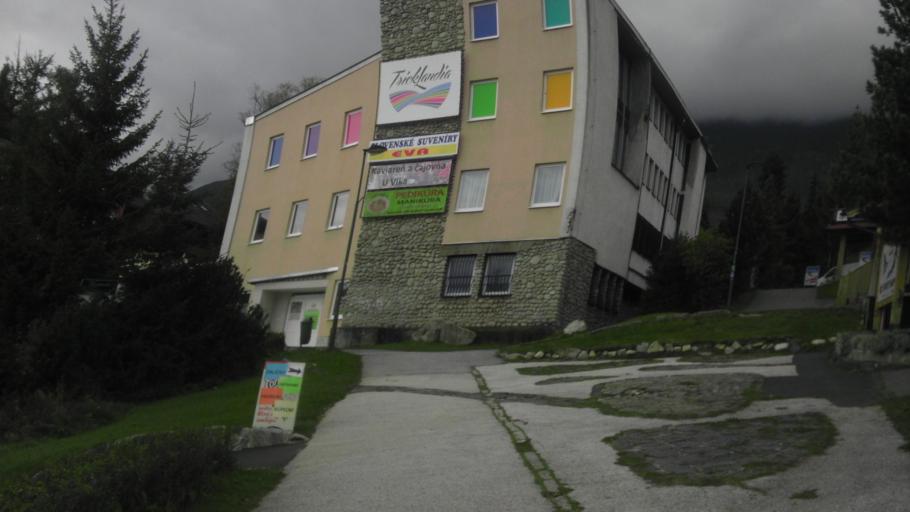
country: SK
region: Presovsky
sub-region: Okres Poprad
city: Vysoke Tatry
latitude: 49.1409
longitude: 20.2249
